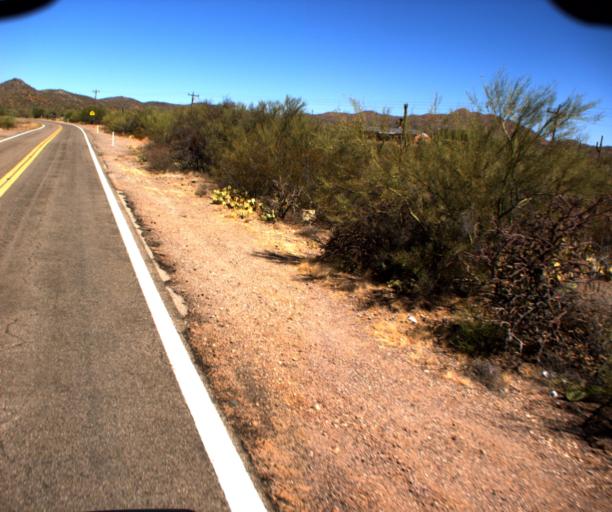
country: US
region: Arizona
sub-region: Pima County
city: Sells
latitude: 32.1673
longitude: -112.1278
